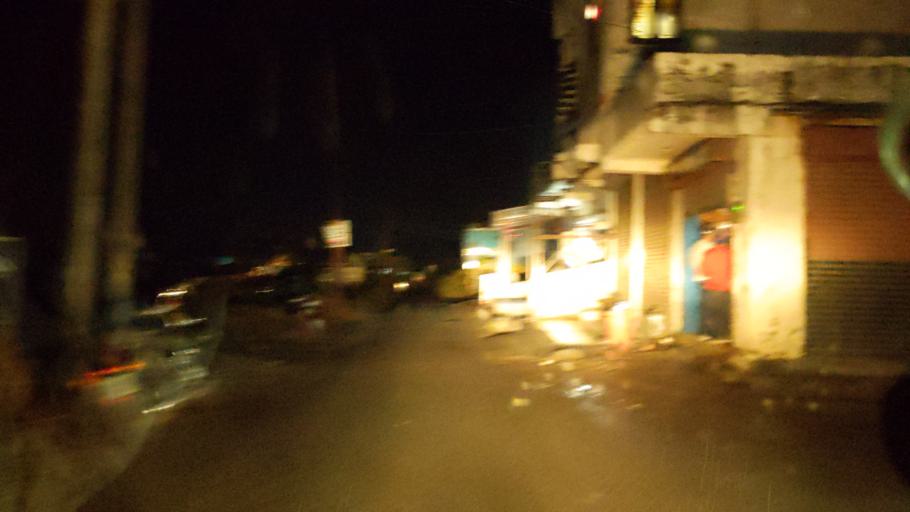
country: IN
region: Uttarakhand
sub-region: Naini Tal
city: Haldwani
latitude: 29.2058
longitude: 79.4988
